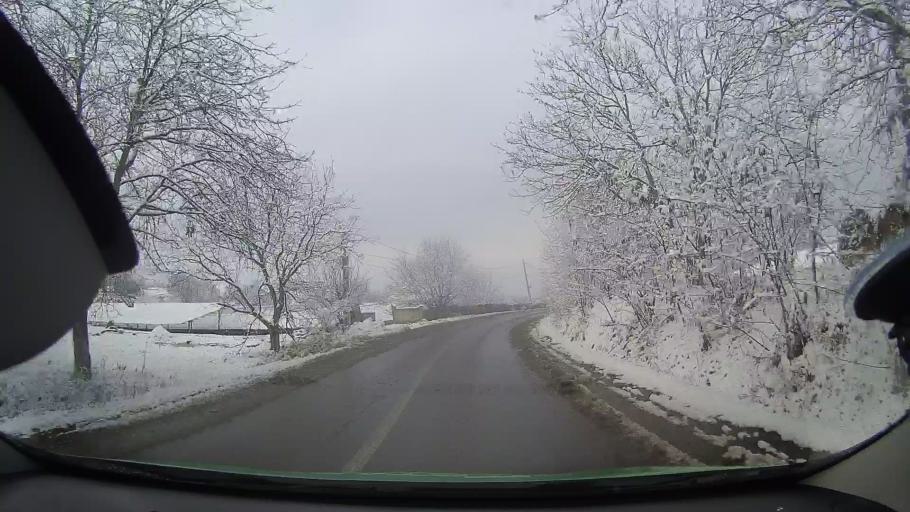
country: RO
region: Mures
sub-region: Comuna Atintis
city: Atintis
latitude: 46.4437
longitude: 24.0907
